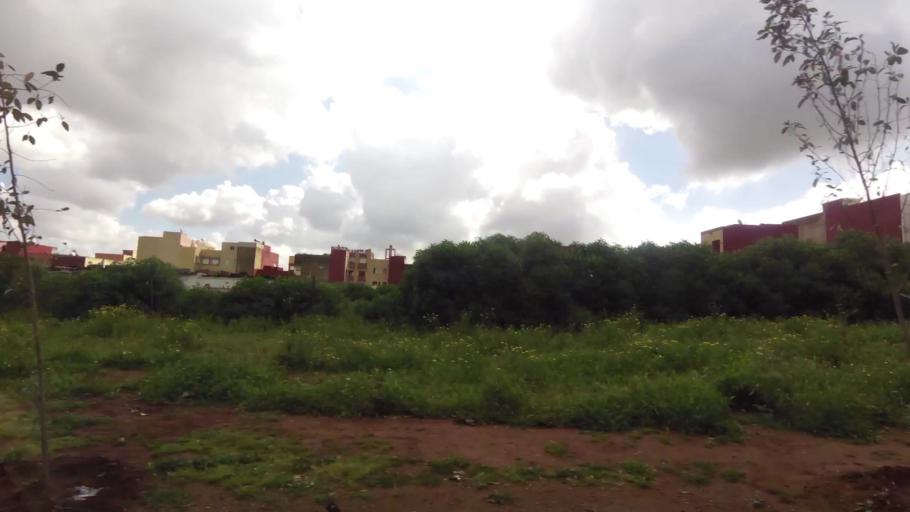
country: MA
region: Grand Casablanca
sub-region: Nouaceur
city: Bouskoura
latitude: 33.5085
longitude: -7.6507
